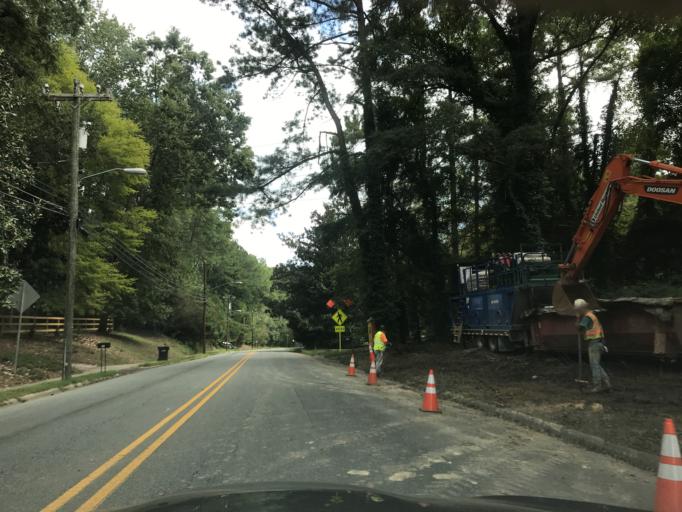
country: US
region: North Carolina
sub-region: Orange County
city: Chapel Hill
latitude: 35.9327
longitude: -79.0405
